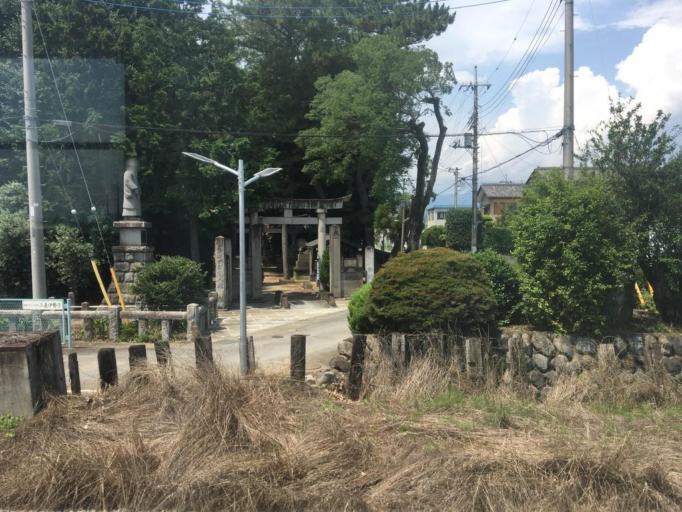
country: JP
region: Gunma
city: Maebashi-shi
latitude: 36.3941
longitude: 139.1076
